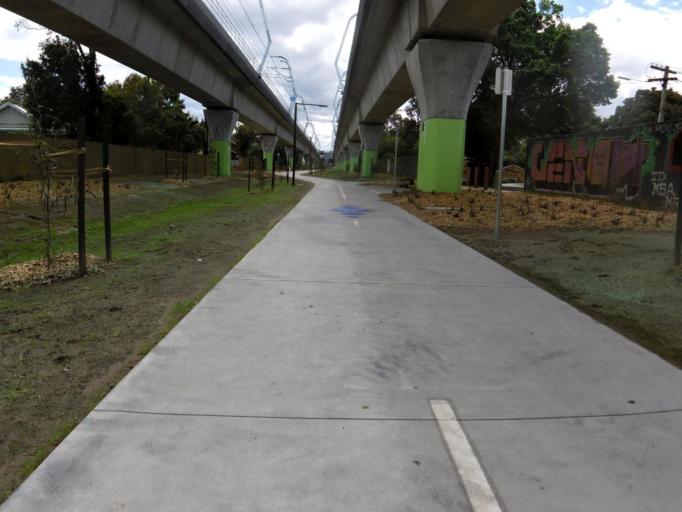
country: AU
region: Victoria
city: Carnegie
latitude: -37.8883
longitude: 145.0632
